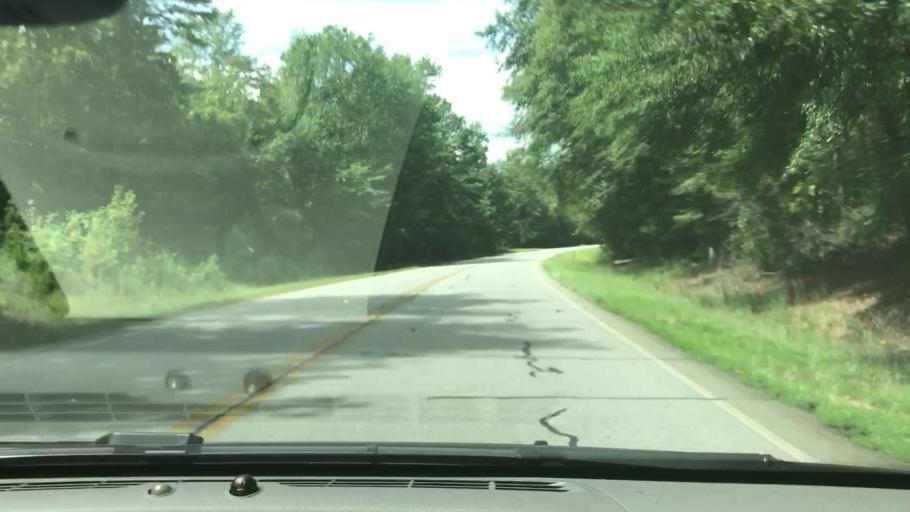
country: US
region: Georgia
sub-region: Stewart County
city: Lumpkin
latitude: 32.1462
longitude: -84.8933
